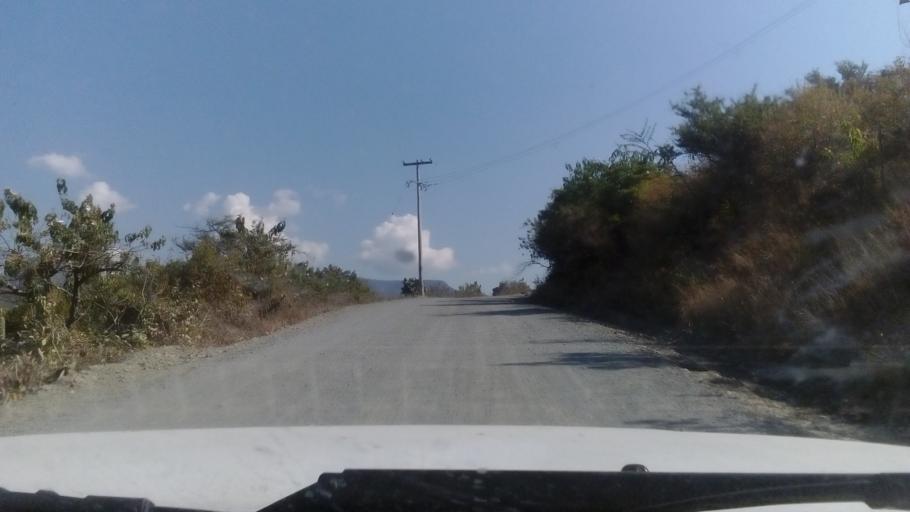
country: MX
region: Guanajuato
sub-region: Leon
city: Medina
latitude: 21.1510
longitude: -101.6017
